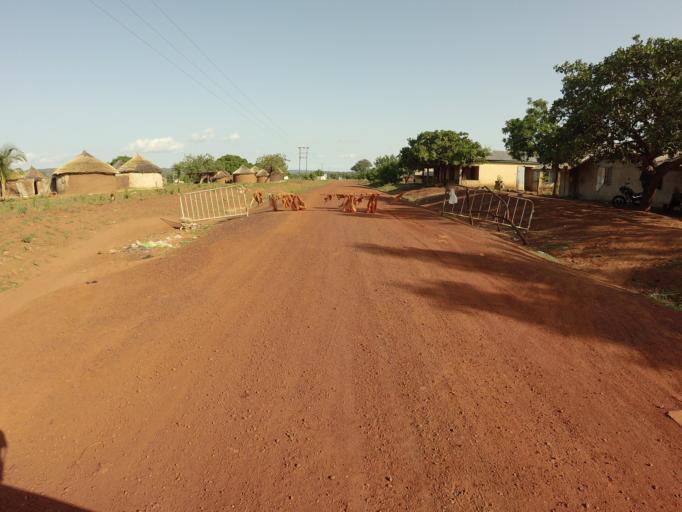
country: GH
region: Upper East
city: Bawku
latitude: 10.6263
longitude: -0.1793
